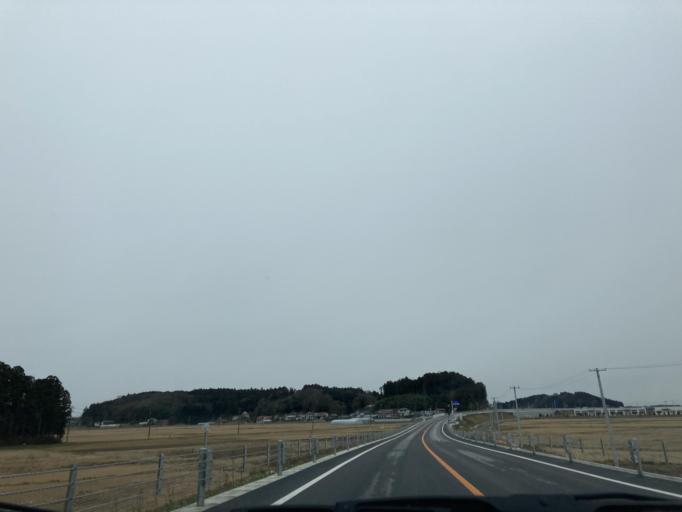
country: JP
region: Miyagi
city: Wakuya
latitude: 38.7016
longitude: 141.1865
